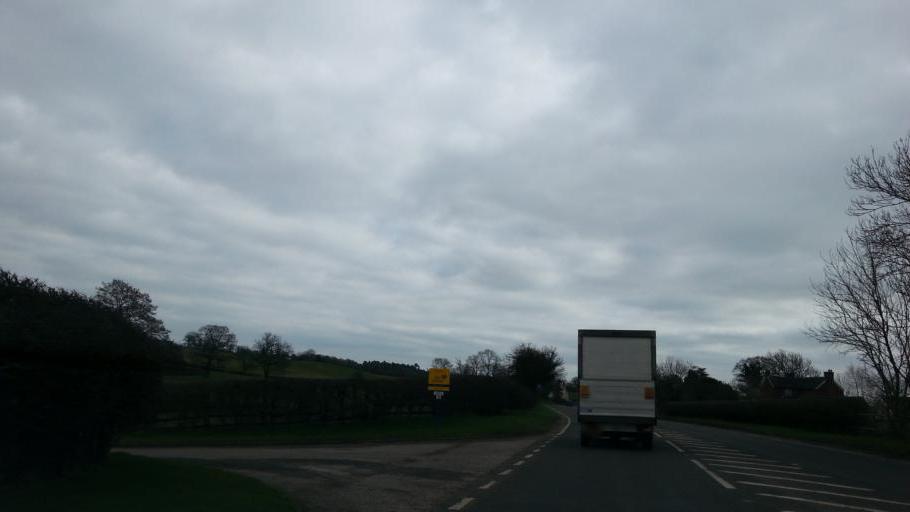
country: GB
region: England
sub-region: Staffordshire
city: Stafford
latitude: 52.8702
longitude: -2.0918
